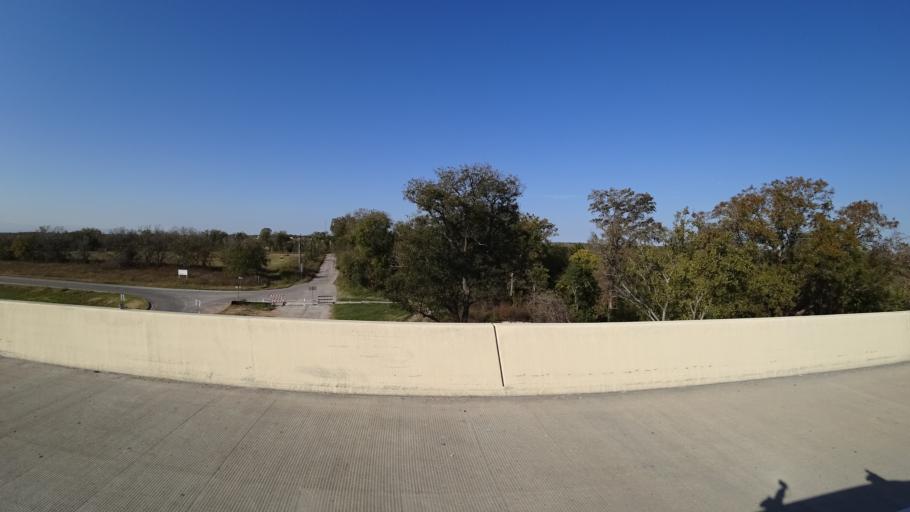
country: US
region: Texas
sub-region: Travis County
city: Hornsby Bend
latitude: 30.2094
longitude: -97.6228
